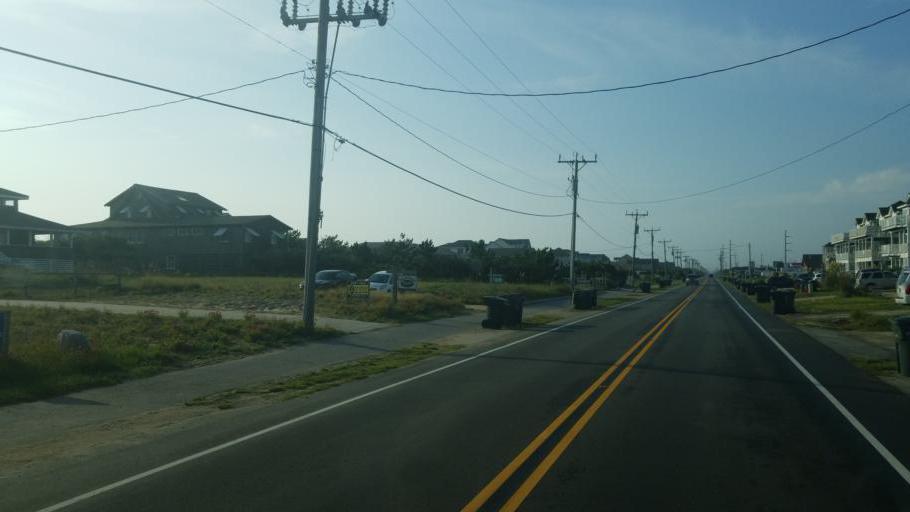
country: US
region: North Carolina
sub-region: Dare County
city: Nags Head
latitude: 35.9675
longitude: -75.6299
